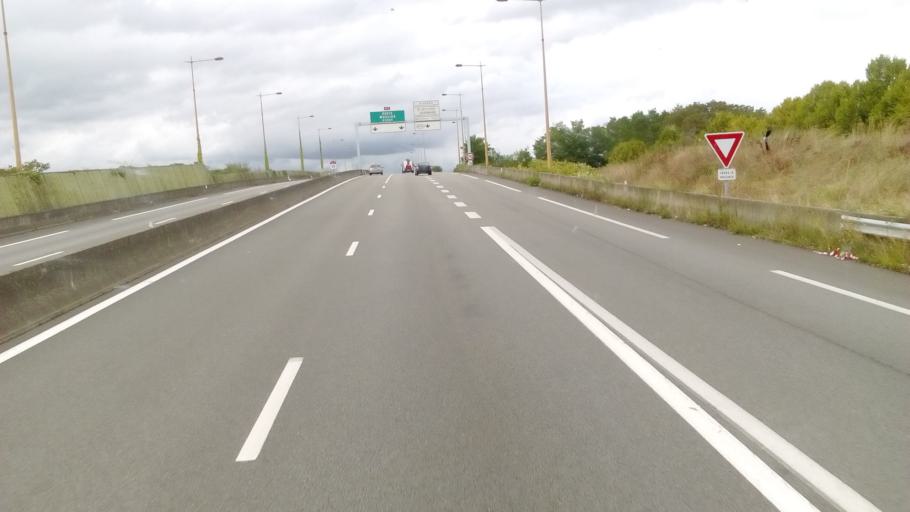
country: FR
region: Rhone-Alpes
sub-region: Departement de la Loire
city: Roanne
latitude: 46.0514
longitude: 4.0827
